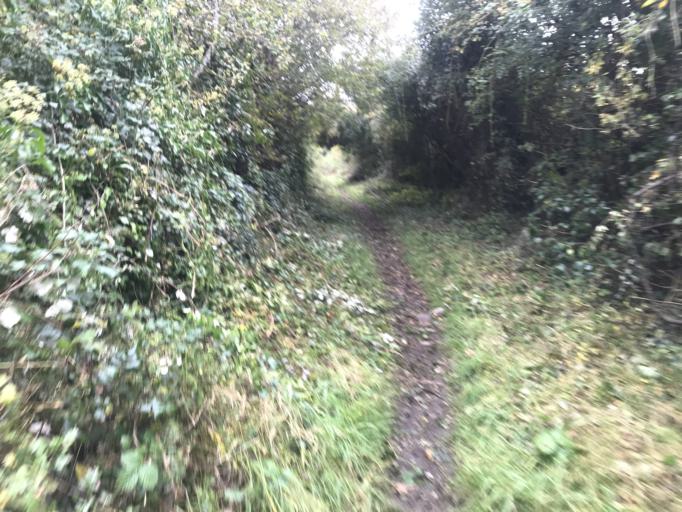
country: IE
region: Connaught
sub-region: County Galway
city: Gaillimh
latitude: 53.2975
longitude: -9.0518
